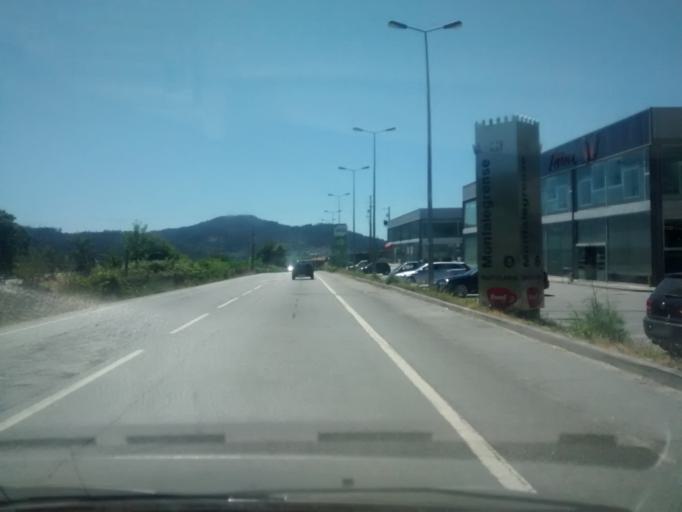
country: PT
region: Braga
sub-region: Braga
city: Braga
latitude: 41.5330
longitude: -8.4667
